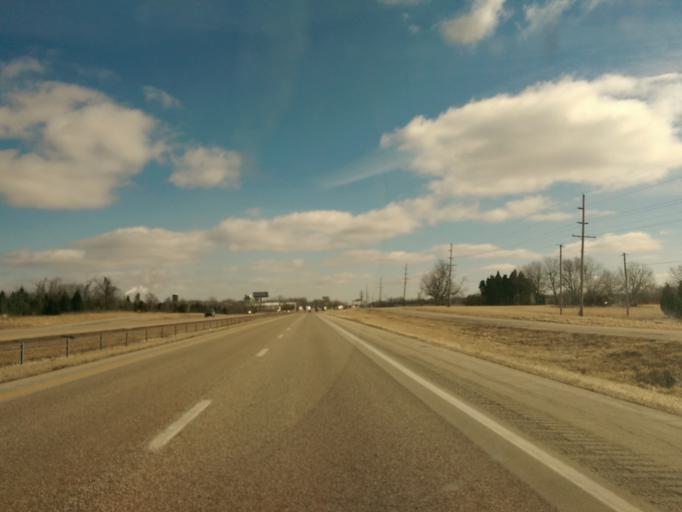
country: US
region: Missouri
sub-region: Montgomery County
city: Montgomery City
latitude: 38.8826
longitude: -91.3976
